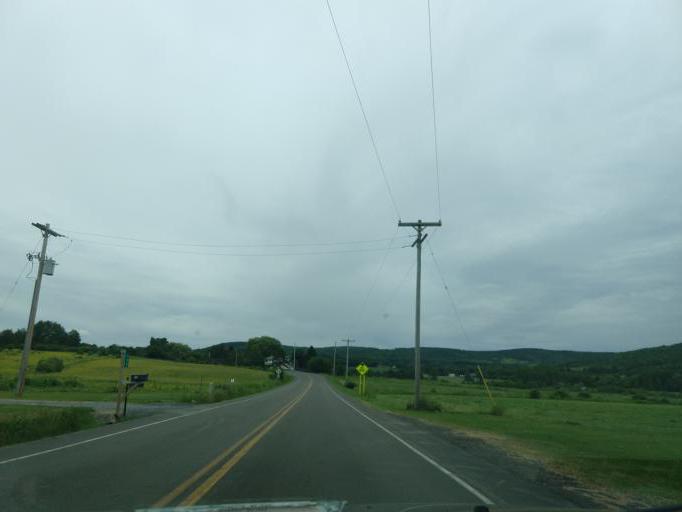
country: US
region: New York
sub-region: Tompkins County
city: Dryden
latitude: 42.4940
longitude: -76.2257
